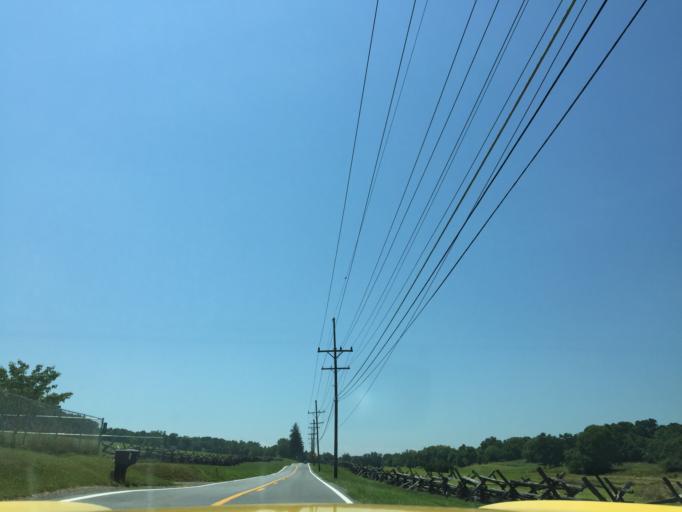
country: US
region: West Virginia
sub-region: Jefferson County
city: Bolivar
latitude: 39.3275
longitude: -77.7654
